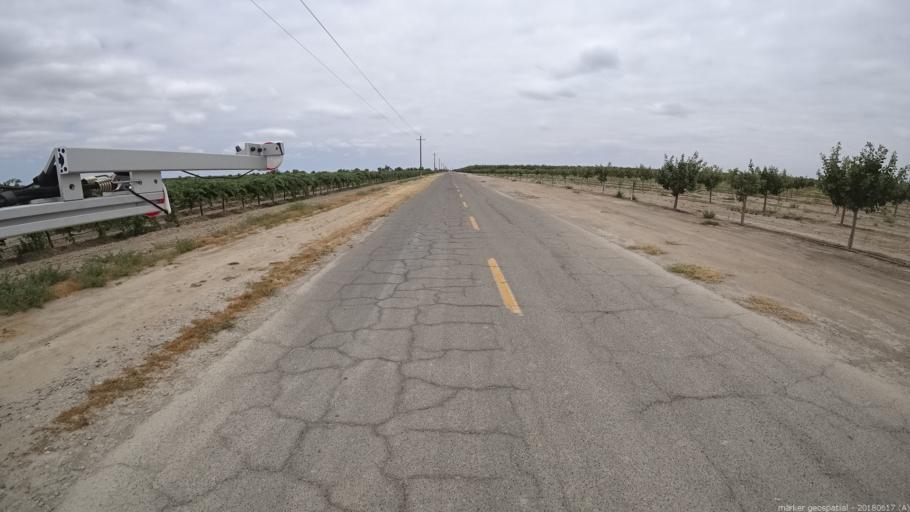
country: US
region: California
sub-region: Madera County
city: Parkwood
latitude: 36.8695
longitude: -120.1649
